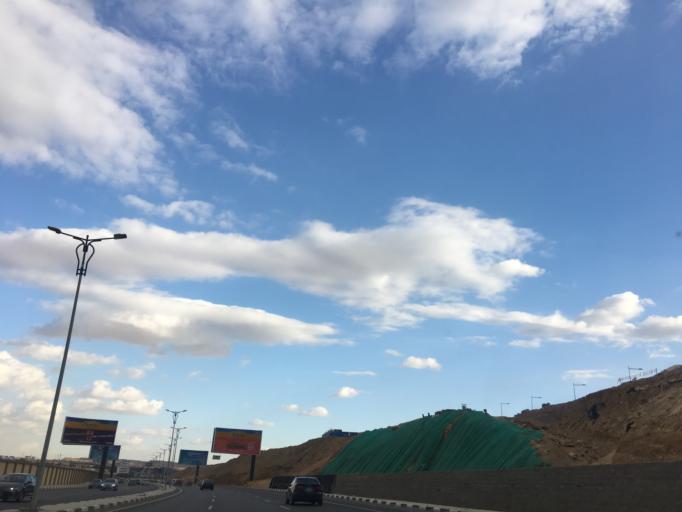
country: EG
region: Muhafazat al Qahirah
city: Cairo
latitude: 30.0282
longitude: 31.3126
